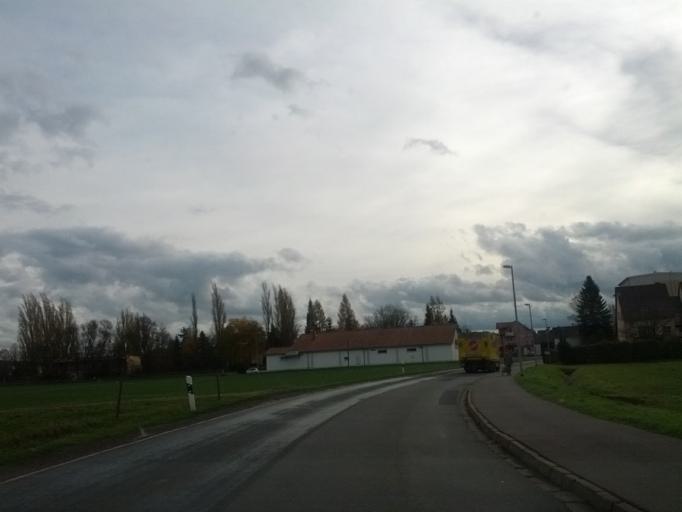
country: DE
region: Thuringia
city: Sonneborn
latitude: 50.9978
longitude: 10.5871
